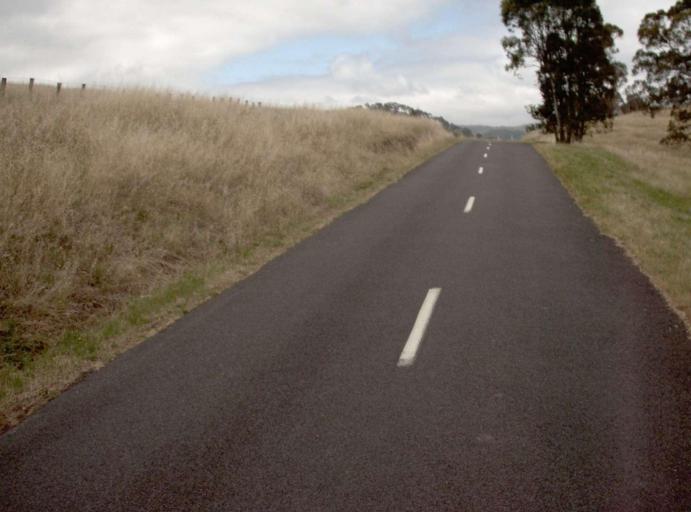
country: AU
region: Victoria
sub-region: Wellington
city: Heyfield
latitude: -37.6844
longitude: 146.6570
